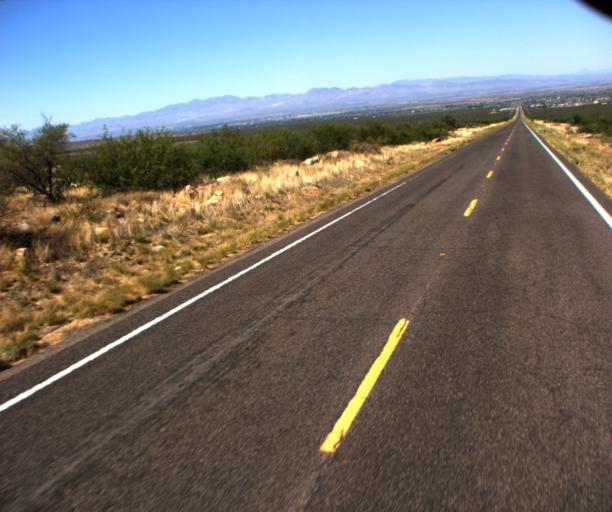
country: US
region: Arizona
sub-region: Graham County
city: Swift Trail Junction
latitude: 32.6946
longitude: -109.7496
